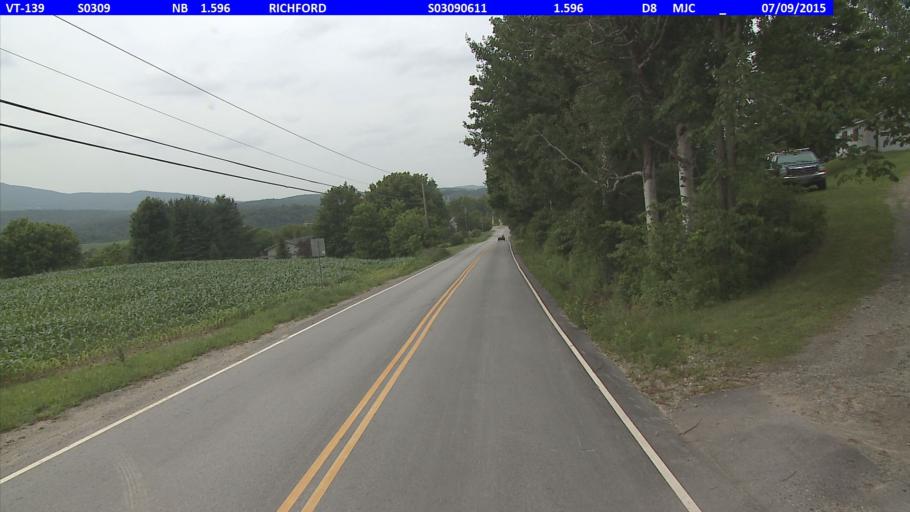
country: US
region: Vermont
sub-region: Franklin County
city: Richford
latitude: 45.0109
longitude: -72.6615
